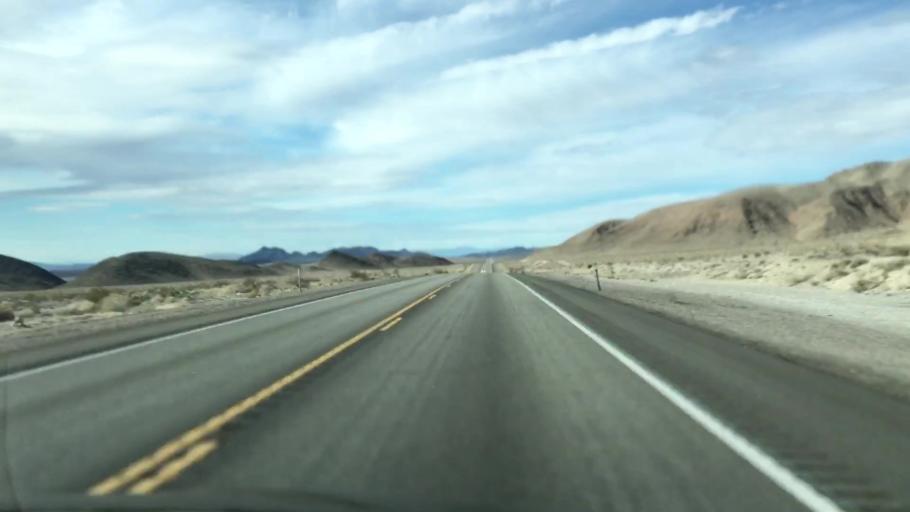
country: US
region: Nevada
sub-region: Nye County
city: Pahrump
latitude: 36.5768
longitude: -116.1930
